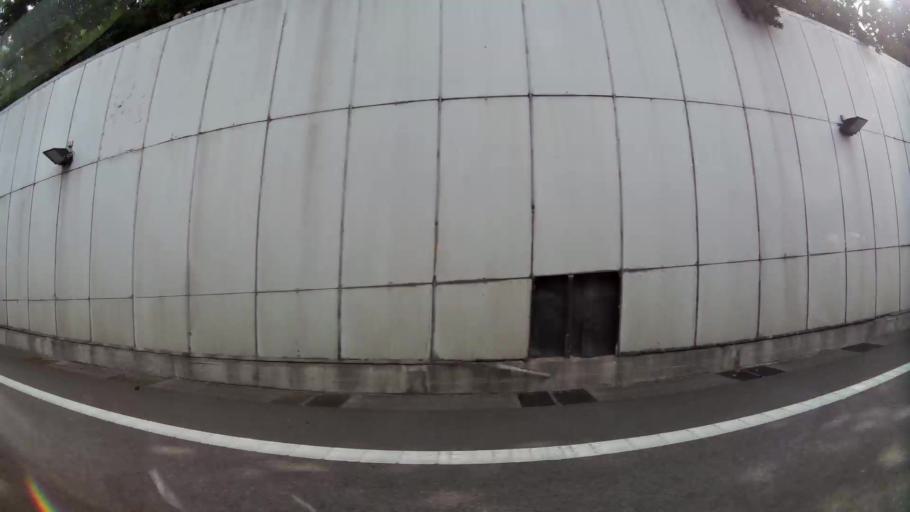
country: MY
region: Johor
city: Johor Bahru
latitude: 1.3398
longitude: 103.6460
